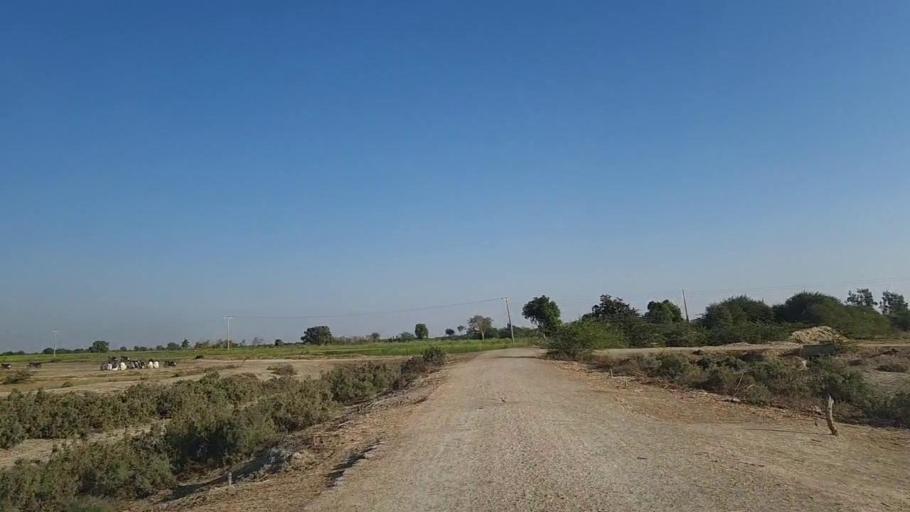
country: PK
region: Sindh
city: Naukot
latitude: 24.9712
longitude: 69.3810
